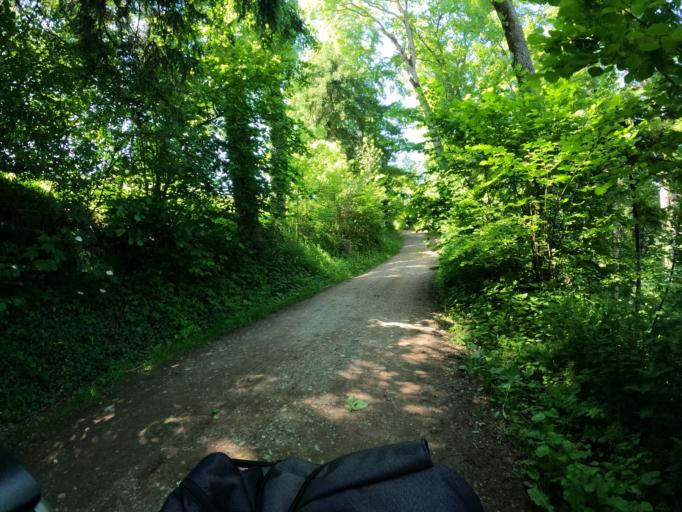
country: CH
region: Zurich
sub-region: Bezirk Affoltern
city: Affoltern / Sonnenberg
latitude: 47.2832
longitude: 8.4797
